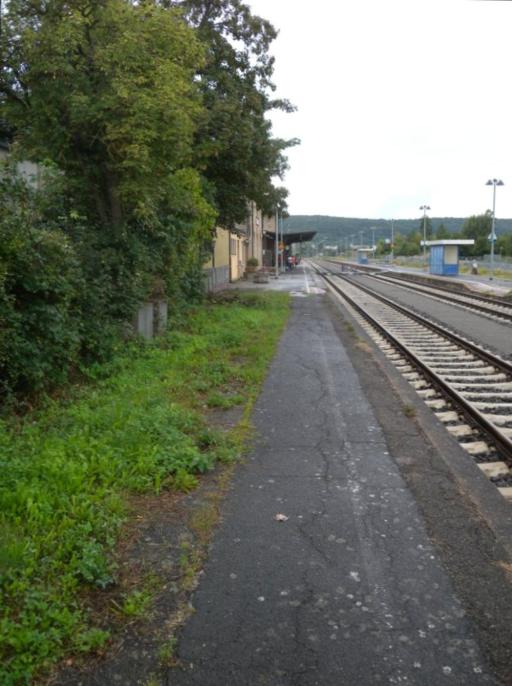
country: DE
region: Baden-Wuerttemberg
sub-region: Regierungsbezirk Stuttgart
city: Bad Mergentheim
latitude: 49.4938
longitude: 9.7729
